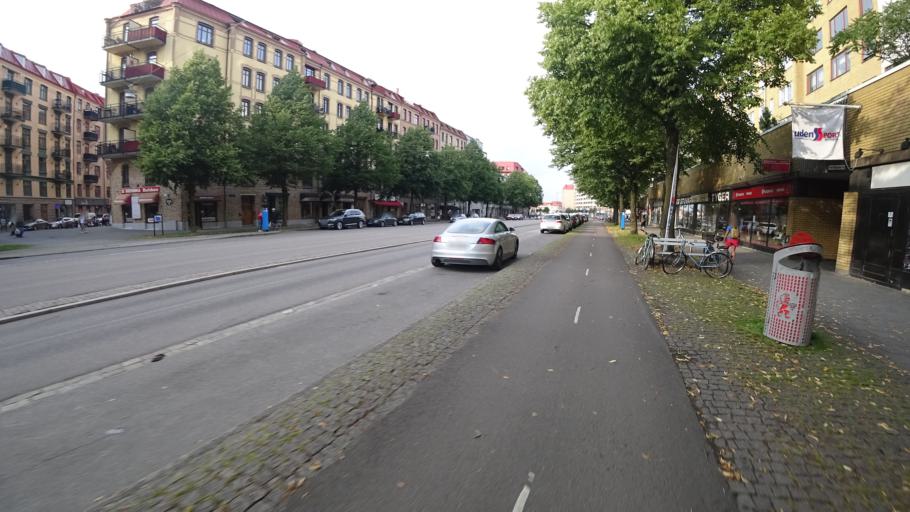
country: SE
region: Vaestra Goetaland
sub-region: Goteborg
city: Goeteborg
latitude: 57.6928
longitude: 11.9563
